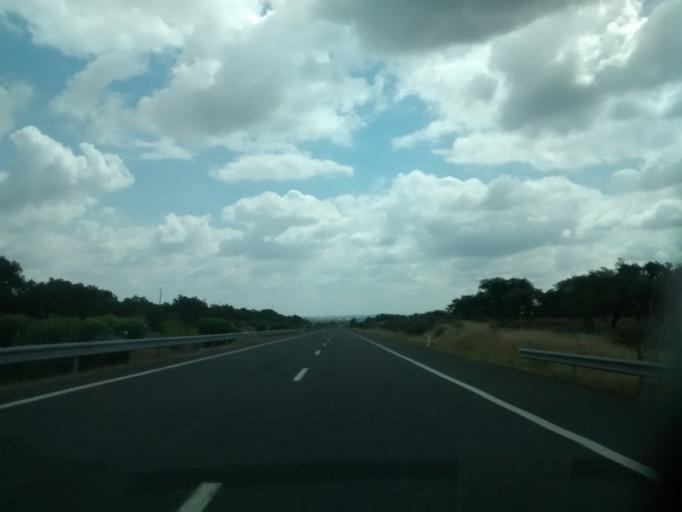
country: PT
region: Evora
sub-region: Evora
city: Evora
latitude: 38.6892
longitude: -7.8127
